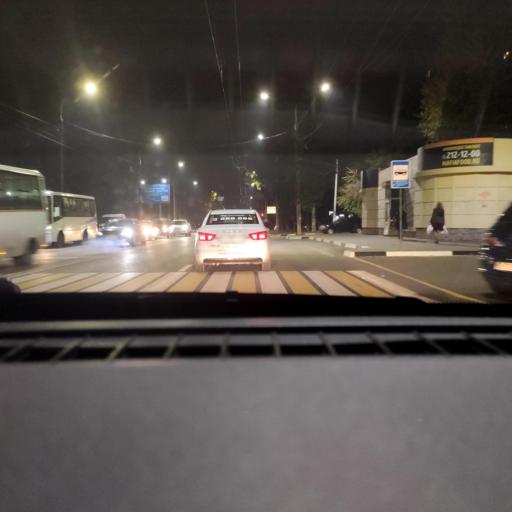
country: RU
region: Voronezj
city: Voronezh
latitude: 51.7022
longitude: 39.1769
